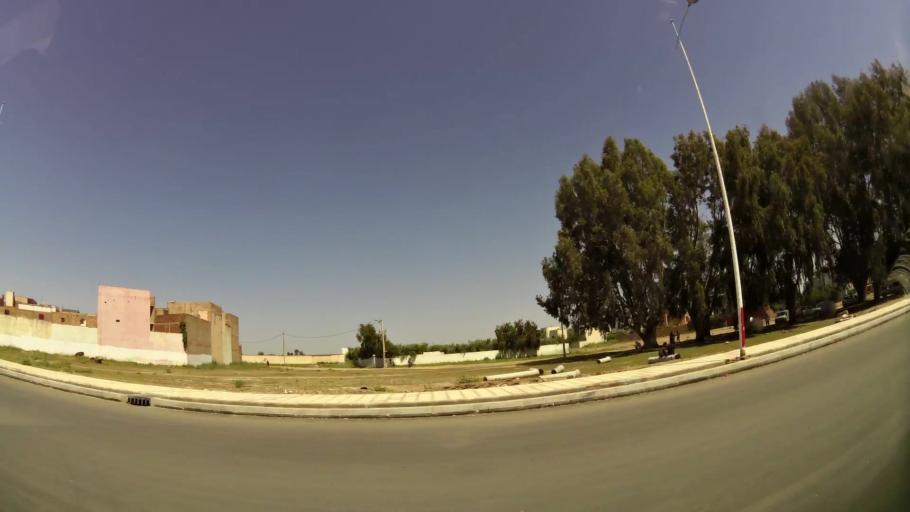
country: MA
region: Rabat-Sale-Zemmour-Zaer
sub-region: Khemisset
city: Khemisset
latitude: 33.8106
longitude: -6.0772
